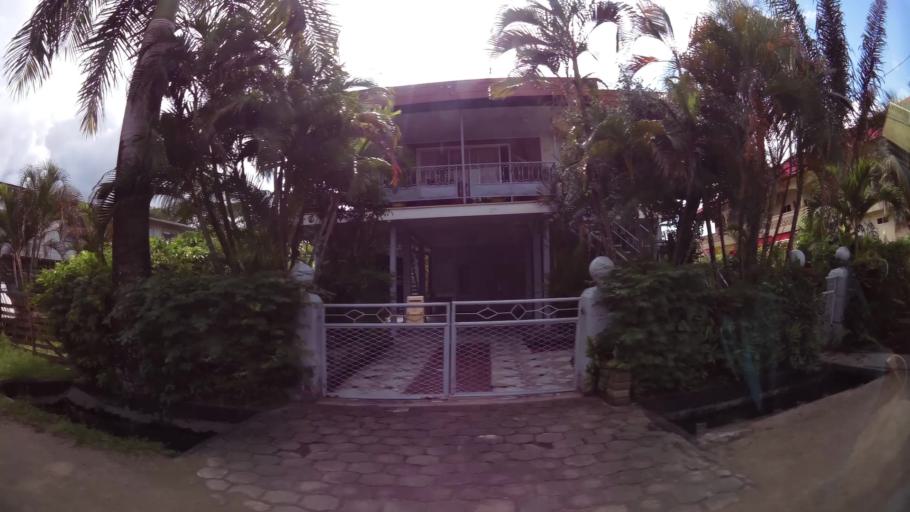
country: SR
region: Paramaribo
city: Paramaribo
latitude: 5.8413
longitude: -55.1560
